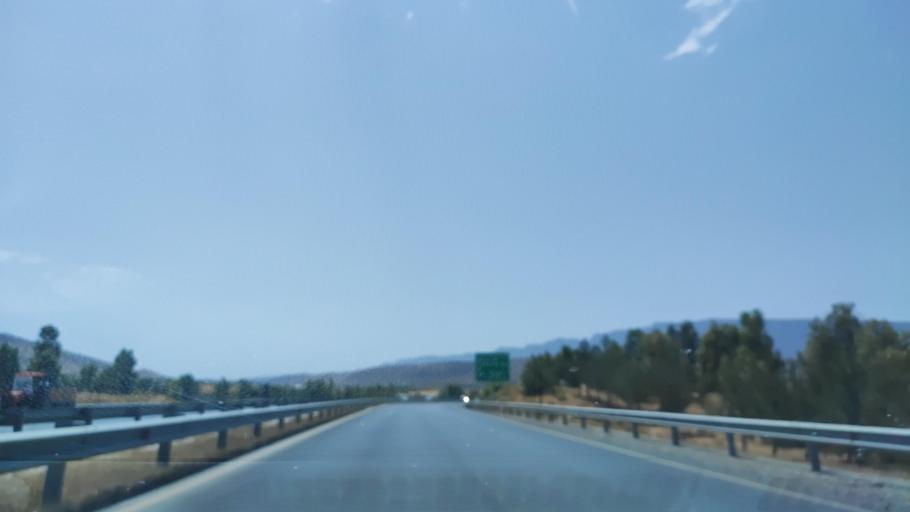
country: IQ
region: Arbil
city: Shaqlawah
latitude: 36.4595
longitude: 44.3842
